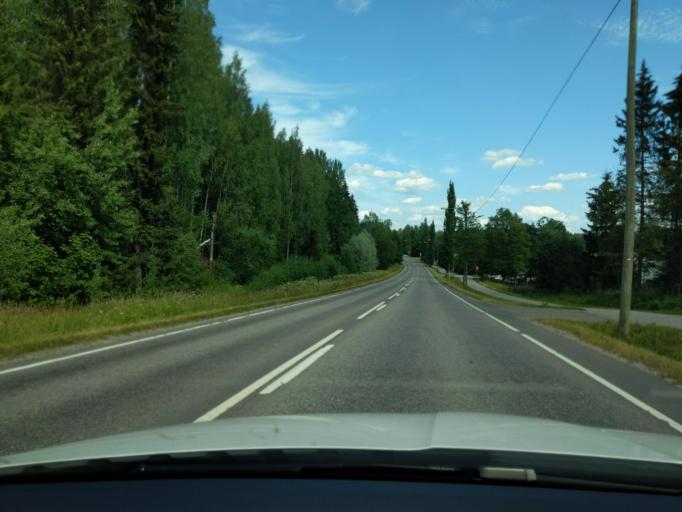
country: FI
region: Paijanne Tavastia
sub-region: Lahti
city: Lahti
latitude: 61.0169
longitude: 25.7159
